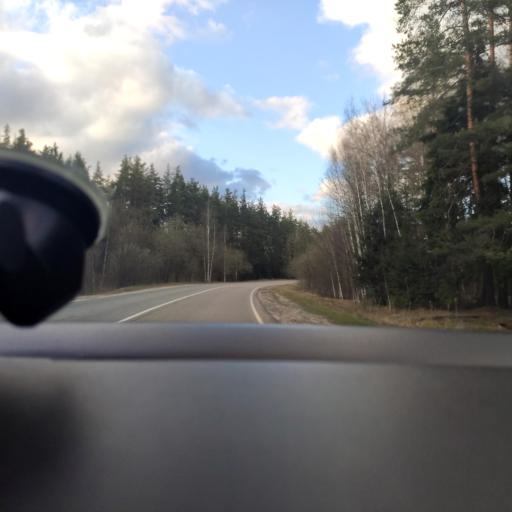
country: RU
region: Moskovskaya
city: Shaturtorf
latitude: 55.4470
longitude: 39.4354
